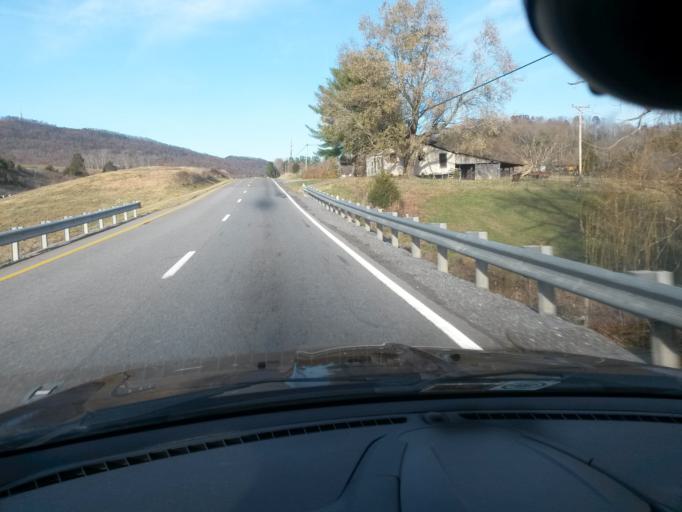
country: US
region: Virginia
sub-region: Botetourt County
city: Fincastle
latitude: 37.6096
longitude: -79.8326
